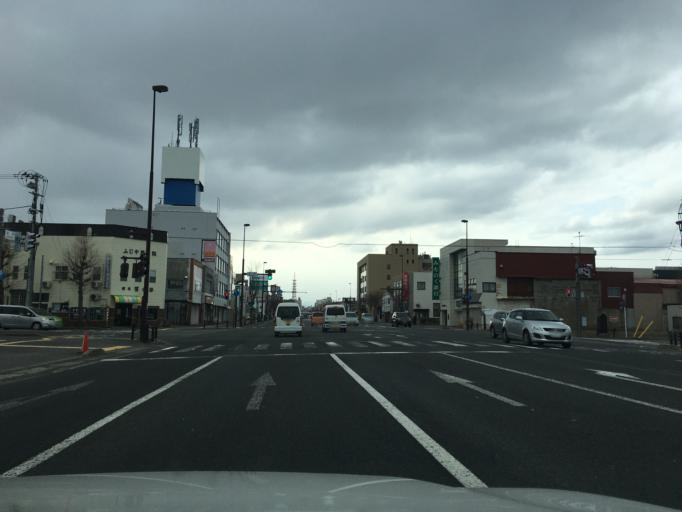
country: JP
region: Aomori
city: Aomori Shi
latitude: 40.8251
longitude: 140.7696
